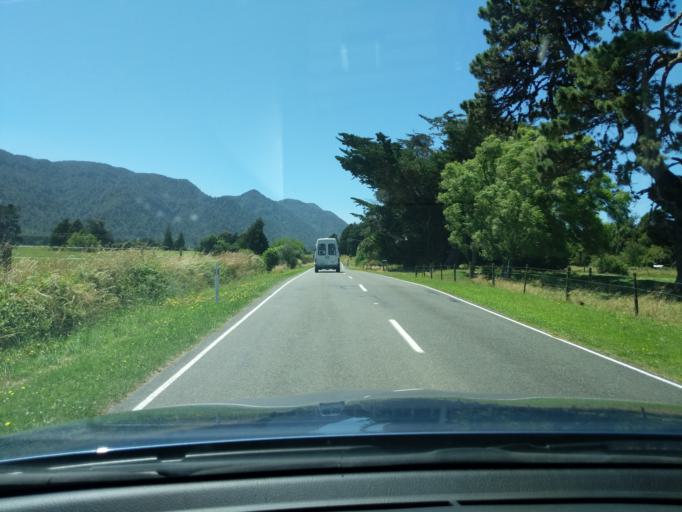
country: NZ
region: Tasman
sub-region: Tasman District
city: Takaka
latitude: -40.6999
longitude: 172.6322
